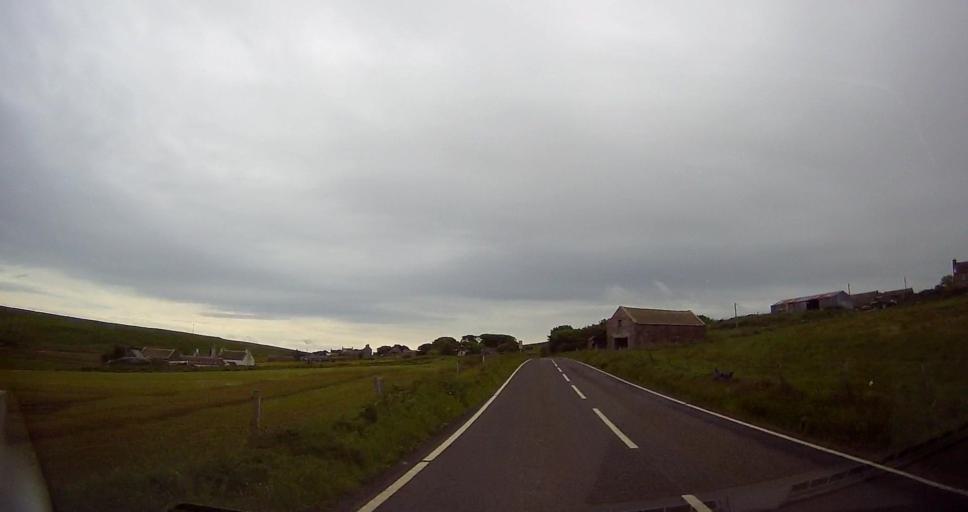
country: GB
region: Scotland
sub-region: Orkney Islands
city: Orkney
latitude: 59.1087
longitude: -3.0952
